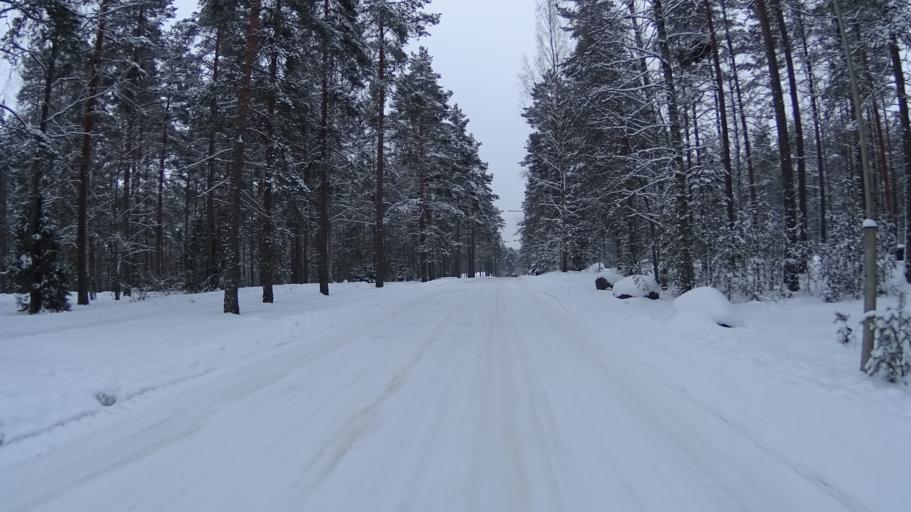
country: FI
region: Uusimaa
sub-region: Helsinki
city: Vihti
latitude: 60.3343
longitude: 24.2990
